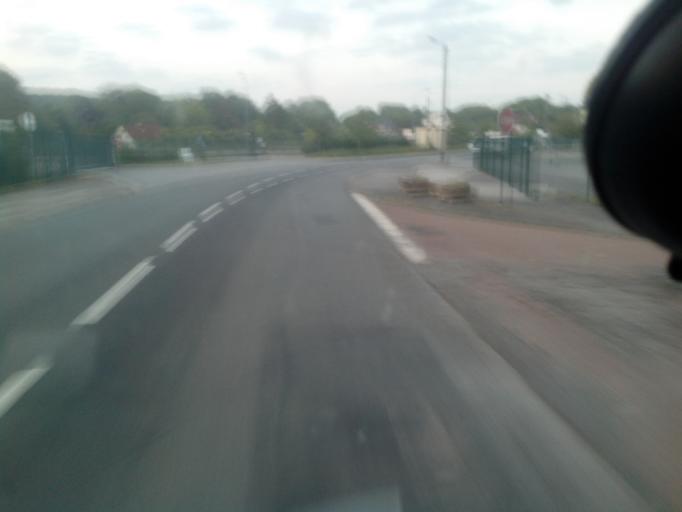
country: FR
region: Nord-Pas-de-Calais
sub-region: Departement du Pas-de-Calais
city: Hesdin
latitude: 50.3770
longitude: 2.0320
